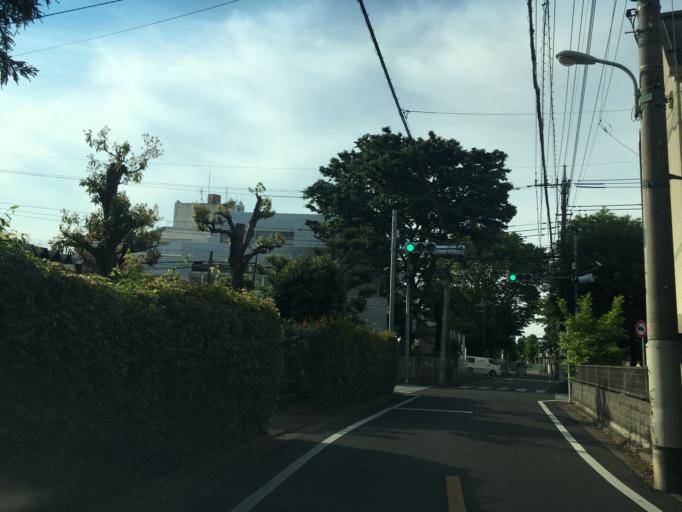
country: JP
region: Tokyo
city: Tanashicho
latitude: 35.7863
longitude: 139.5257
